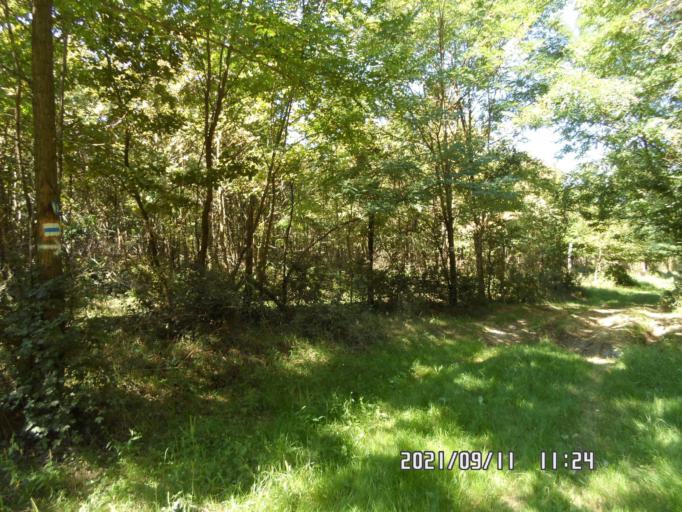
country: HU
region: Zala
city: Zalalovo
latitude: 46.7338
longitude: 16.7071
